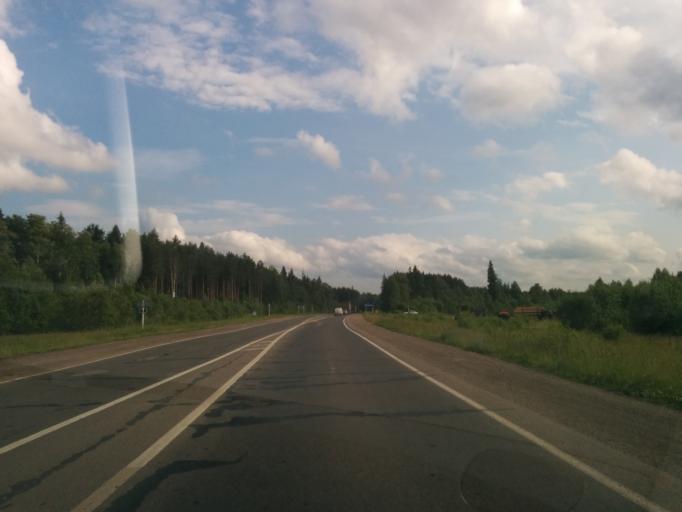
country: RU
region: Perm
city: Polazna
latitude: 58.1155
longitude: 56.4261
